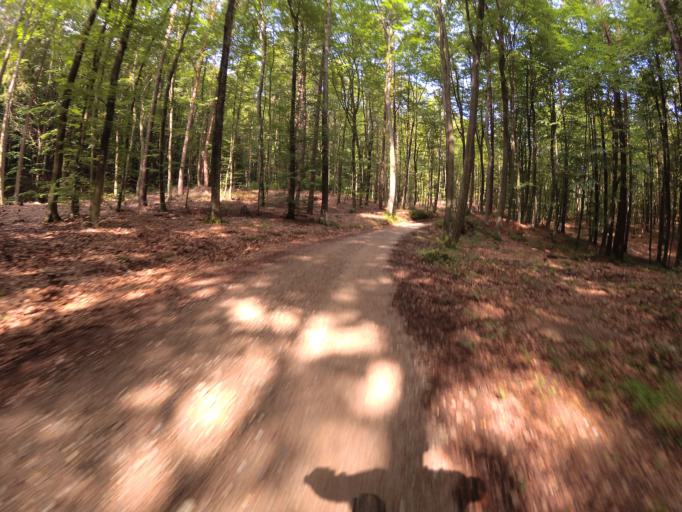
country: PL
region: Pomeranian Voivodeship
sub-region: Gdynia
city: Wielki Kack
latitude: 54.4945
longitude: 18.4773
